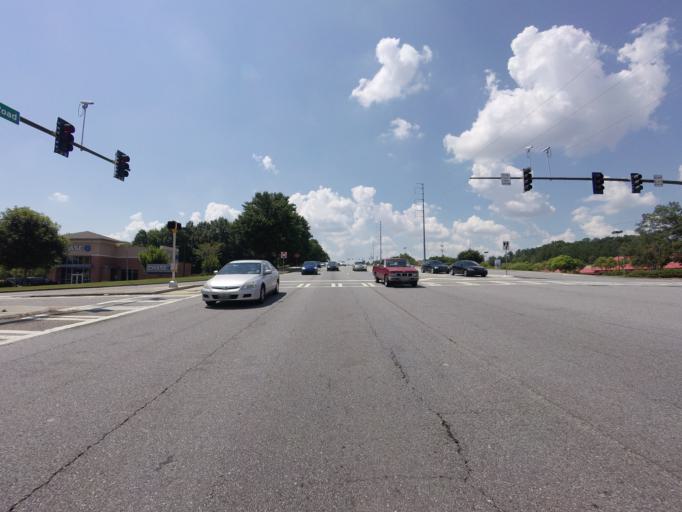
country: US
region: Georgia
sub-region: Fulton County
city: Johns Creek
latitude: 34.0163
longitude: -84.1878
